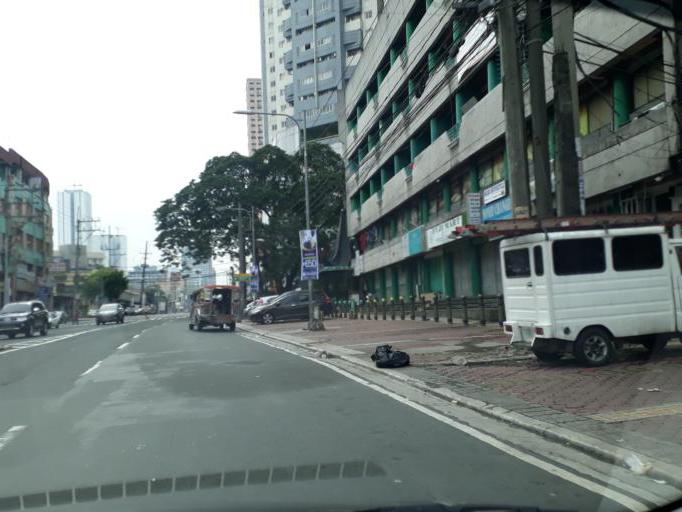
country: PH
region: Calabarzon
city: Del Monte
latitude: 14.6367
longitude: 121.0266
